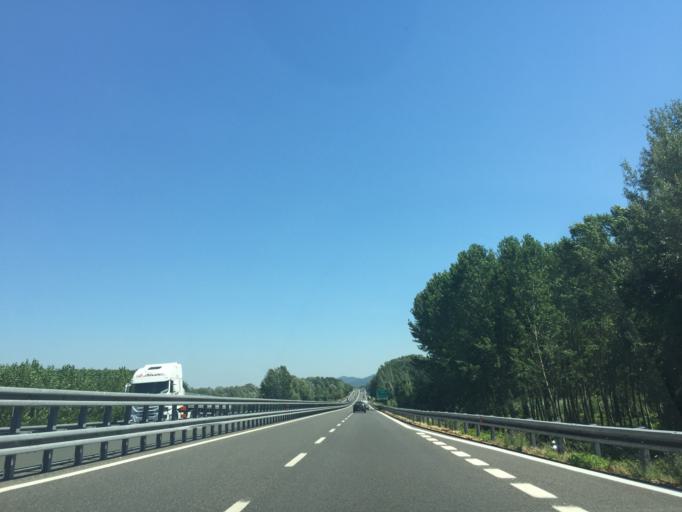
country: IT
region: Tuscany
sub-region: Provincia di Lucca
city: Lucca
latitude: 43.8455
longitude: 10.4503
